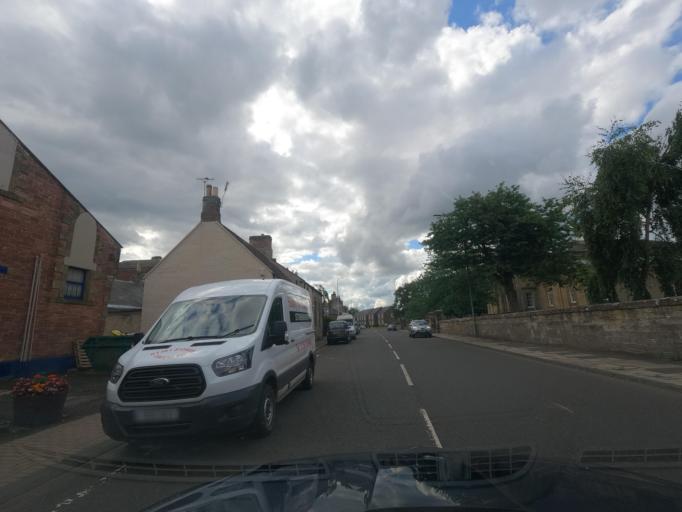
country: GB
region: Scotland
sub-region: The Scottish Borders
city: Kelso
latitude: 55.7069
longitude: -2.4599
